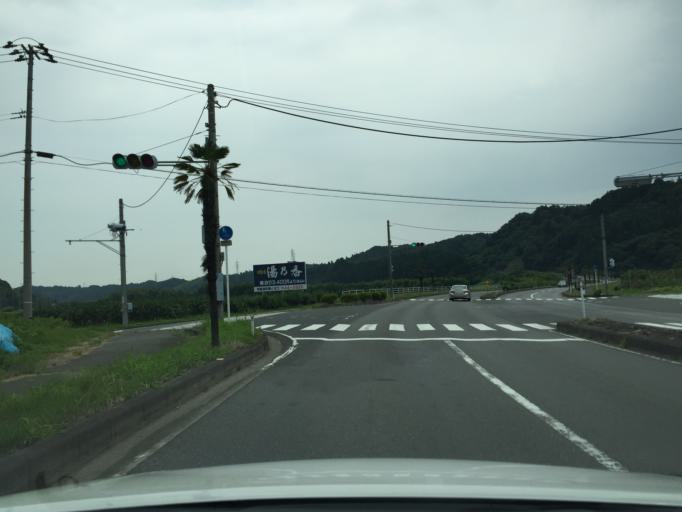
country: JP
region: Fukushima
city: Iwaki
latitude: 36.9930
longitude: 140.8254
